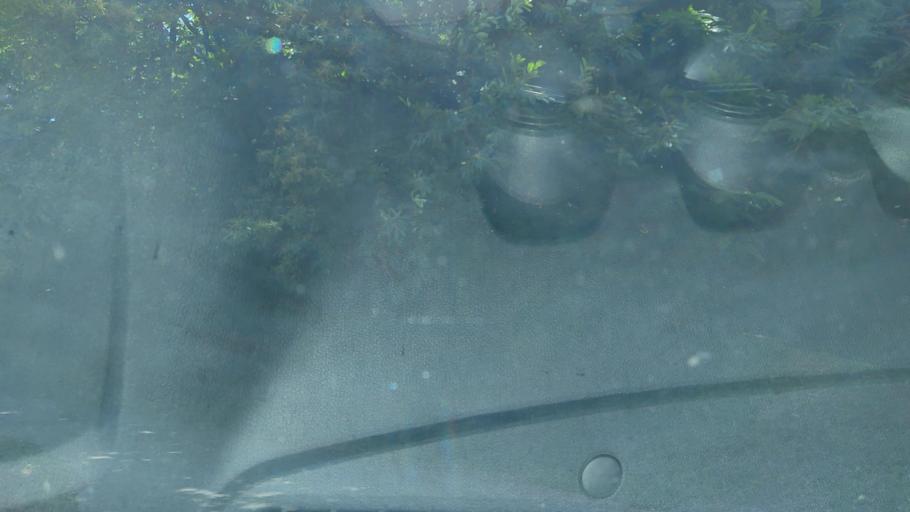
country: FR
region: Rhone-Alpes
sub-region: Departement de la Savoie
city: Aiton
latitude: 45.5050
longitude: 6.2824
